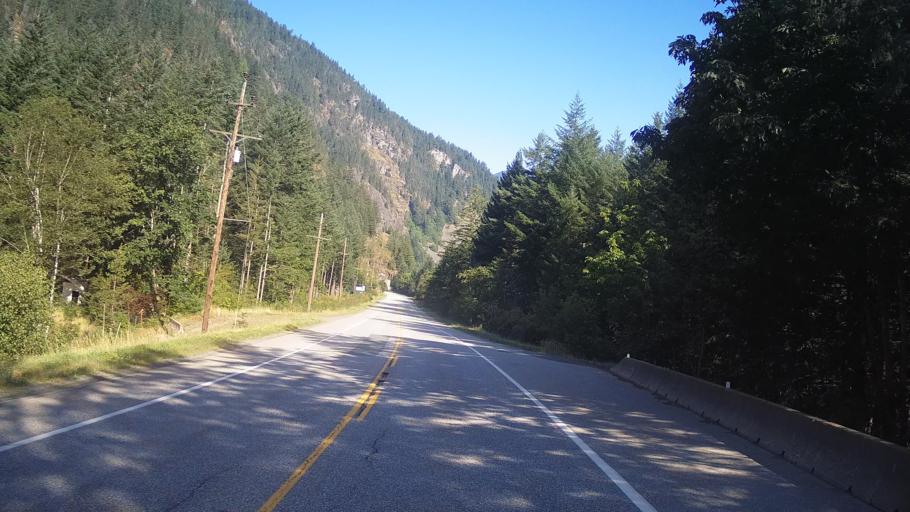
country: CA
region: British Columbia
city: Hope
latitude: 49.6331
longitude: -121.3956
